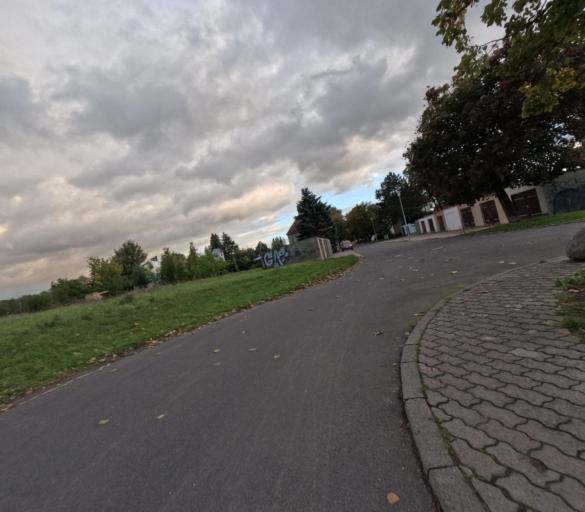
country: DE
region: Saxony
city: Markranstadt
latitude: 51.2868
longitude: 12.2312
